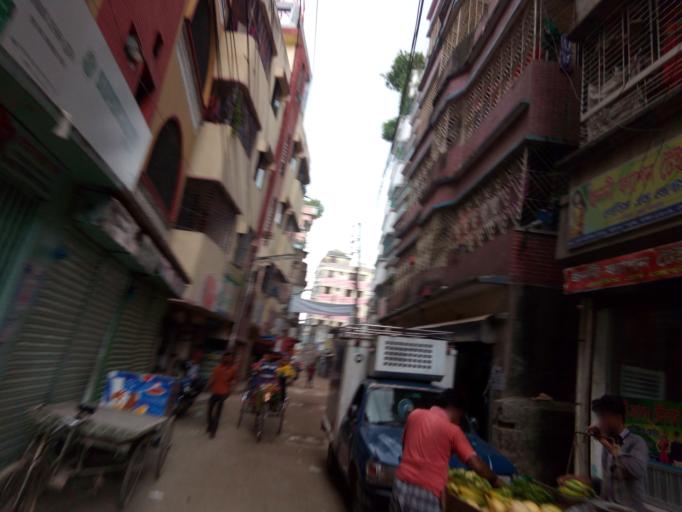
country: BD
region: Dhaka
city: Paltan
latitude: 23.7237
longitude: 90.4354
